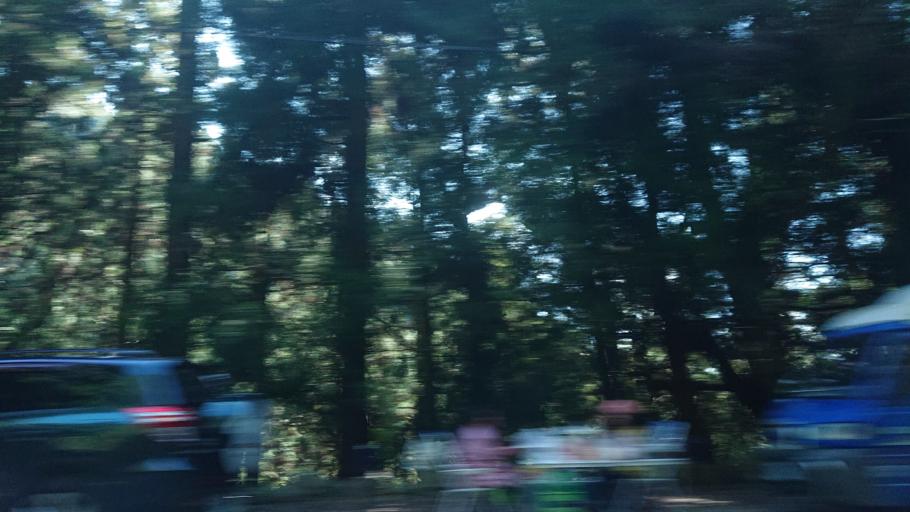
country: TW
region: Taiwan
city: Lugu
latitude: 23.4851
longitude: 120.8299
